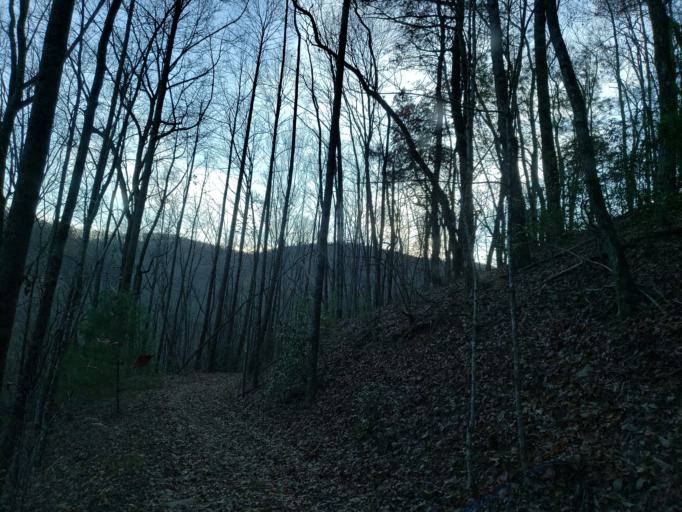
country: US
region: Georgia
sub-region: Lumpkin County
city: Dahlonega
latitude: 34.6654
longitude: -84.1078
